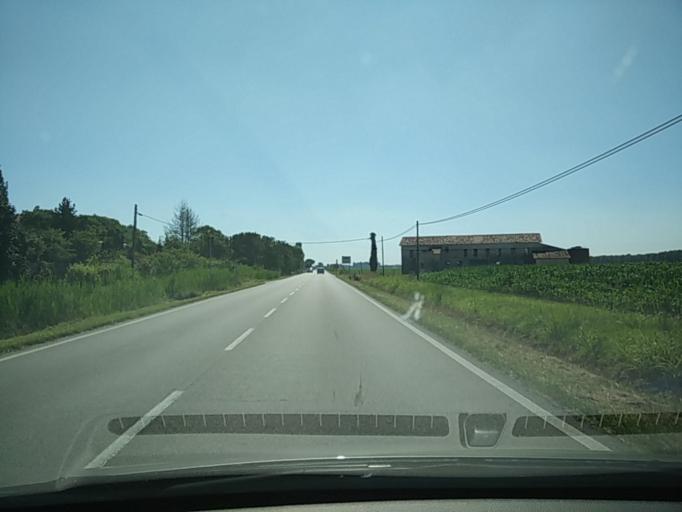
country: IT
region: Veneto
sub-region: Provincia di Venezia
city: Passarella
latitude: 45.6390
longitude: 12.6220
